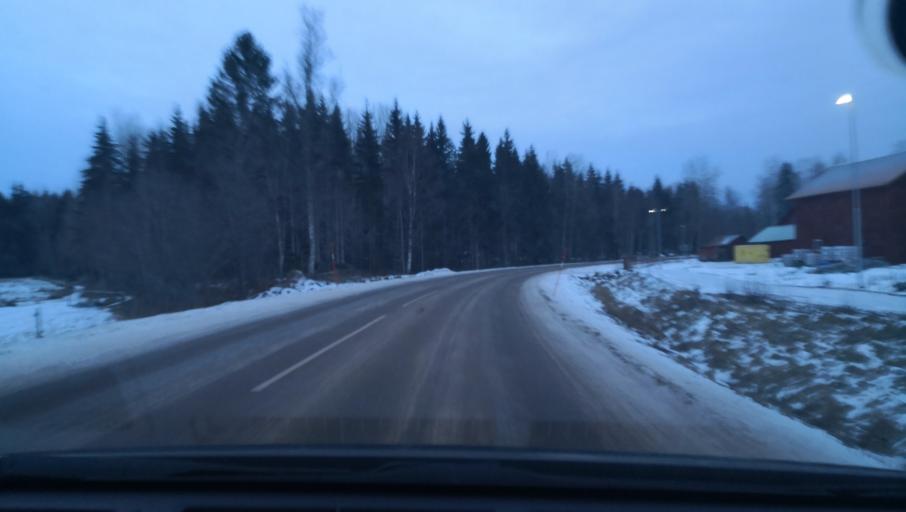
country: SE
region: Dalarna
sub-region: Avesta Kommun
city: Horndal
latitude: 60.1991
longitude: 16.4615
